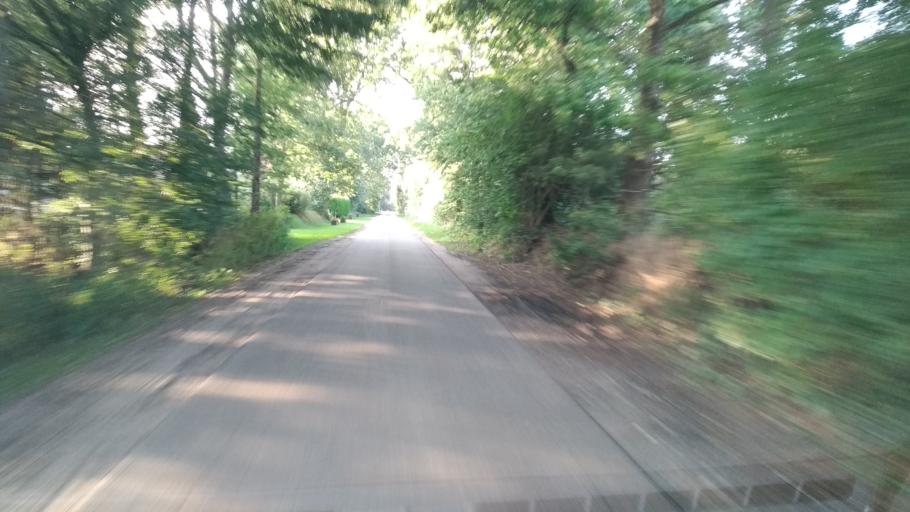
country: DE
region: Schleswig-Holstein
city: Klein Bennebek
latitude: 54.4179
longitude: 9.4566
